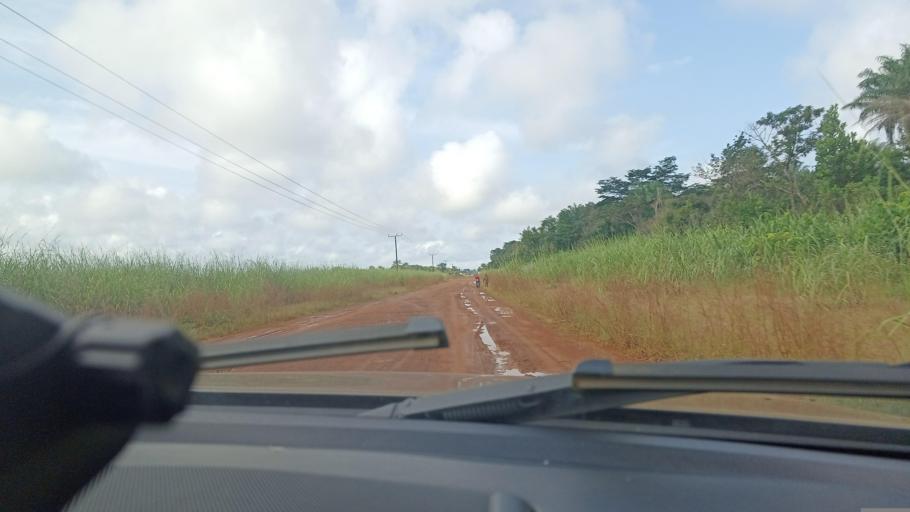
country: LR
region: Grand Cape Mount
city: Robertsport
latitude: 6.6974
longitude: -11.0999
